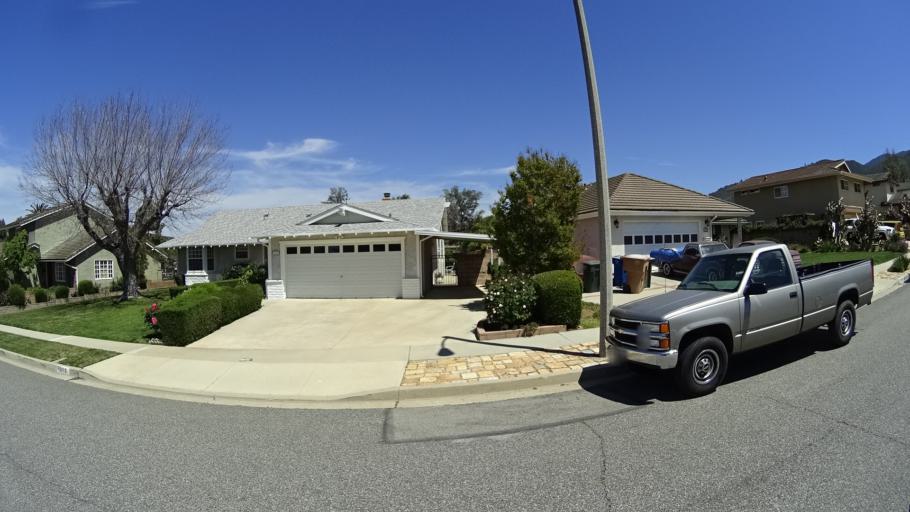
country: US
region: California
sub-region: Ventura County
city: Casa Conejo
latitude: 34.1584
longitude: -118.9556
